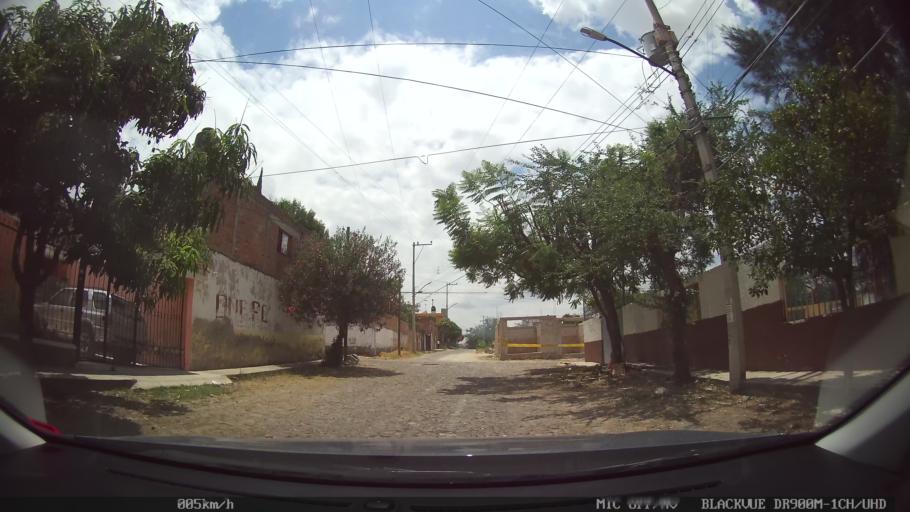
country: MX
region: Jalisco
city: Tlaquepaque
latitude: 20.6362
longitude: -103.2654
